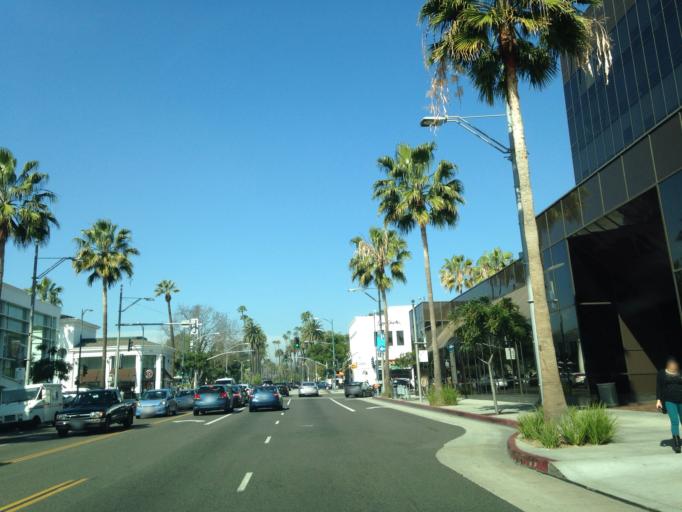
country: US
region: California
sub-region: Los Angeles County
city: Beverly Hills
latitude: 34.0708
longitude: -118.4028
